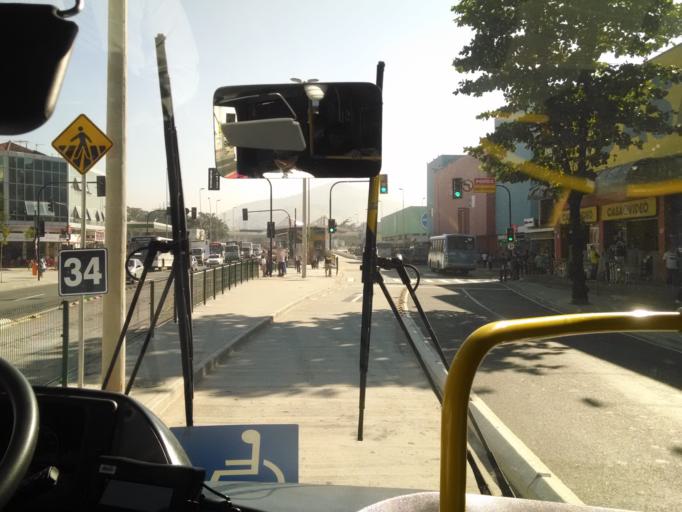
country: BR
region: Rio de Janeiro
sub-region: Sao Joao De Meriti
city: Sao Joao de Meriti
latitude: -22.9256
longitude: -43.3738
